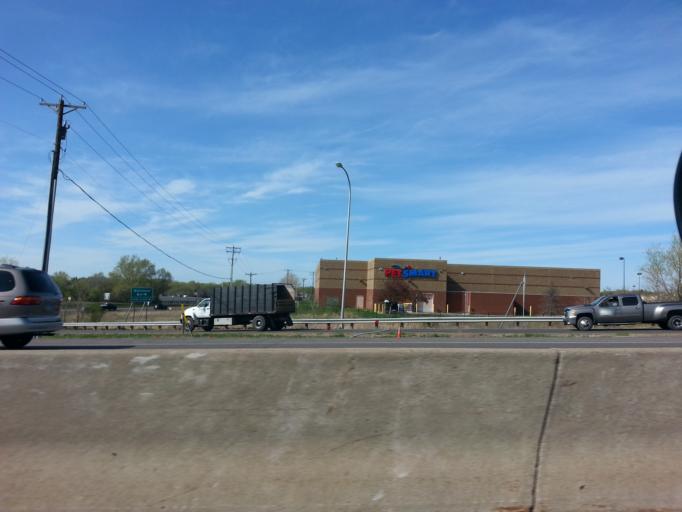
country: US
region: Minnesota
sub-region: Ramsey County
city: North Saint Paul
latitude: 45.0116
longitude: -93.0200
